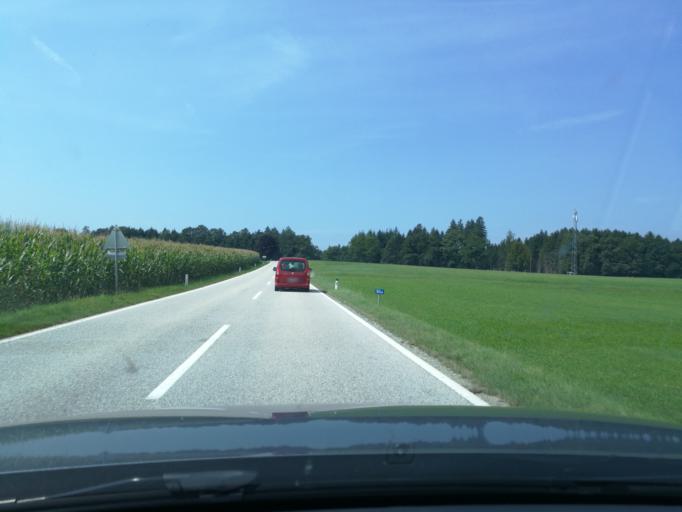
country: AT
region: Upper Austria
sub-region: Politischer Bezirk Grieskirchen
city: Grieskirchen
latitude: 48.3500
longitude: 13.7263
